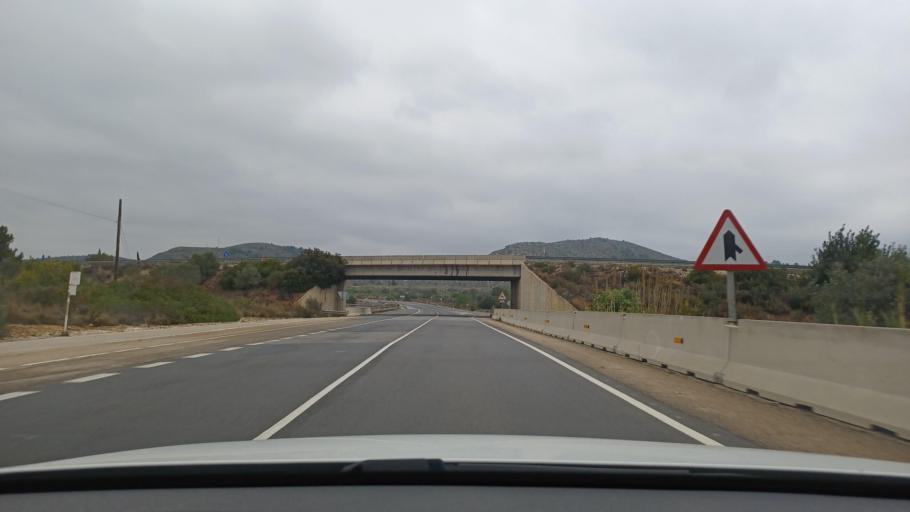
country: ES
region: Valencia
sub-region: Provincia de Castello
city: Alcala de Xivert
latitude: 40.2667
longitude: 0.2405
